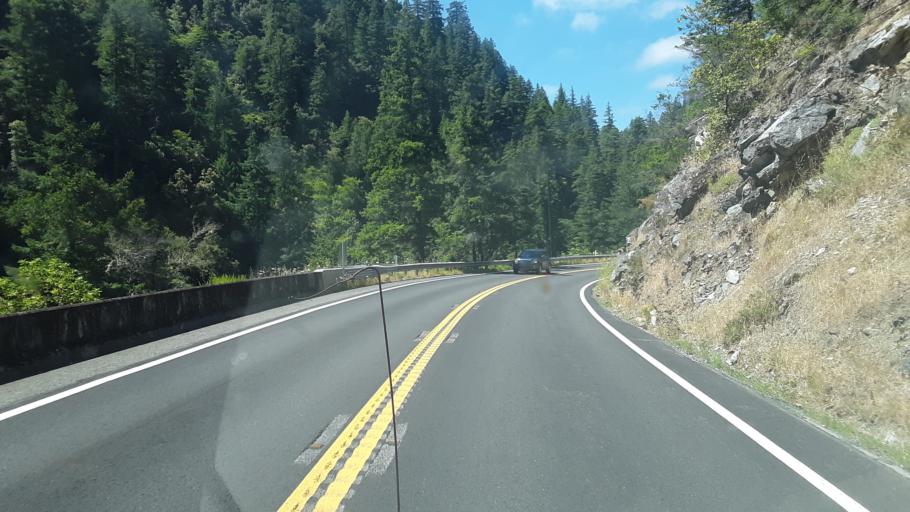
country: US
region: California
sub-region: Del Norte County
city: Bertsch-Oceanview
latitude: 41.8168
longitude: -124.0386
